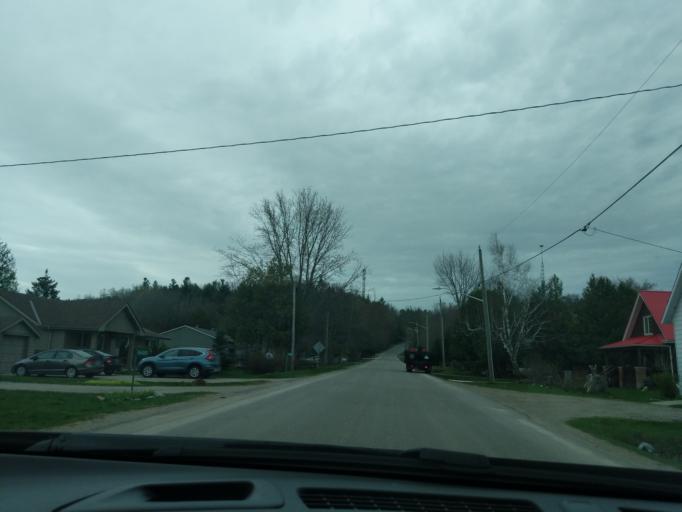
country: CA
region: Ontario
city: Orangeville
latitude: 44.0206
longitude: -79.9688
